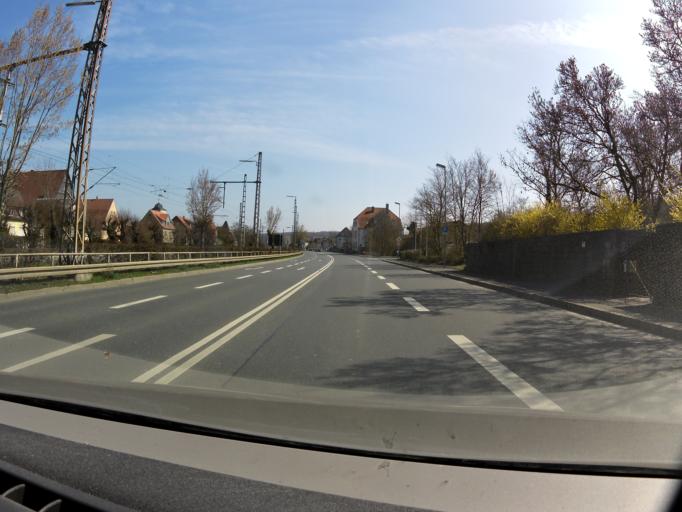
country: DE
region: Bavaria
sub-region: Regierungsbezirk Unterfranken
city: Ochsenfurt
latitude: 49.6628
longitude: 10.0631
